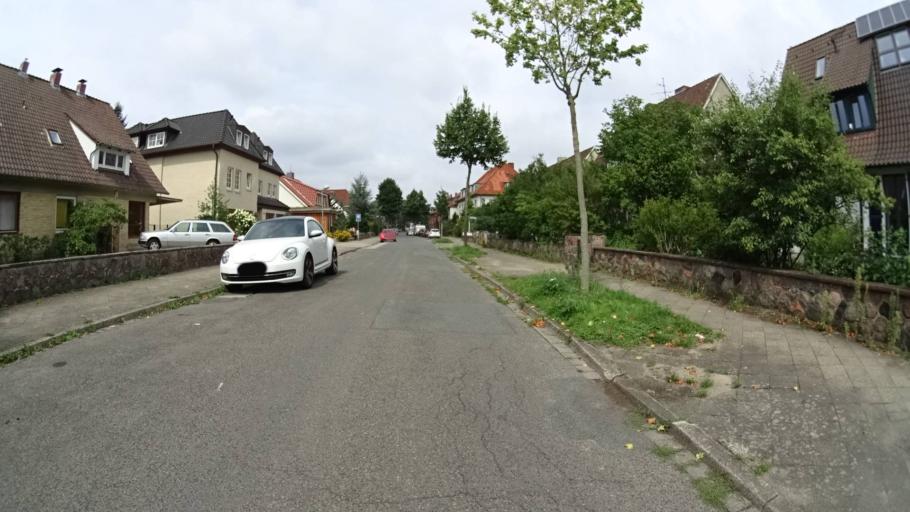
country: DE
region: Lower Saxony
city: Lueneburg
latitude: 53.2377
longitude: 10.4120
